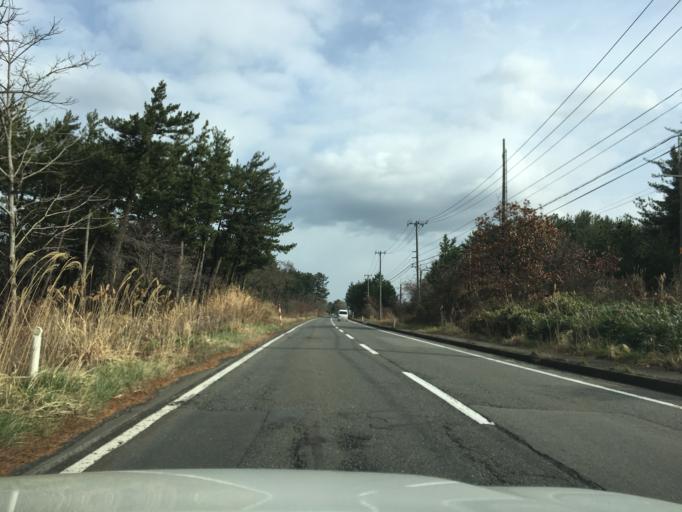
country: JP
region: Yamagata
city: Yuza
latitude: 39.2302
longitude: 139.9071
